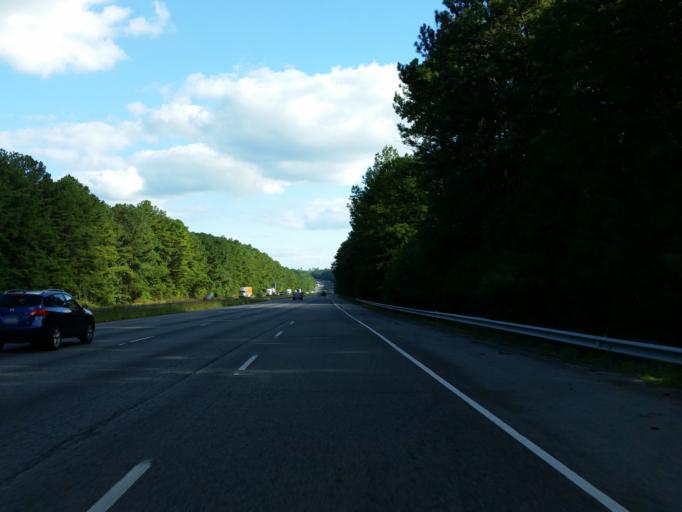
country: US
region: Georgia
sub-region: Butts County
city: Indian Springs
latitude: 33.1612
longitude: -84.0380
